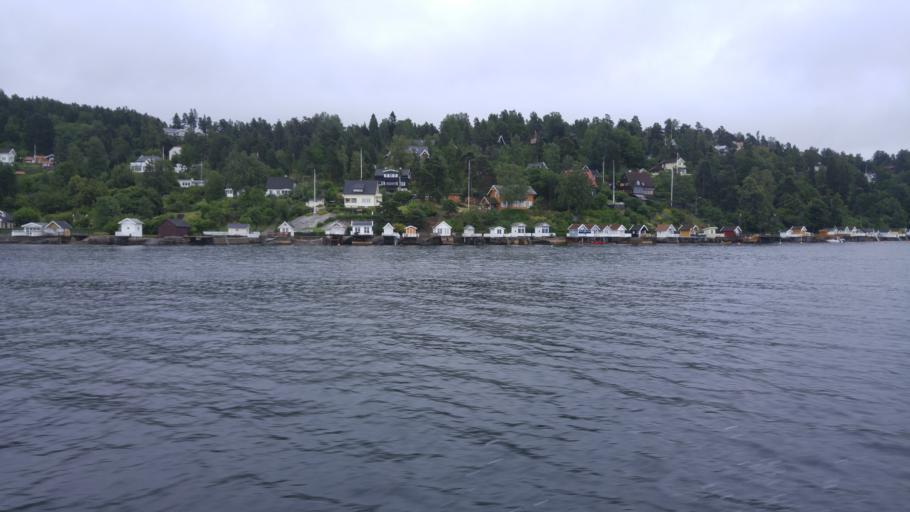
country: NO
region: Akershus
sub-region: Nesodden
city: Nesoddtangen
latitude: 59.8586
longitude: 10.6474
